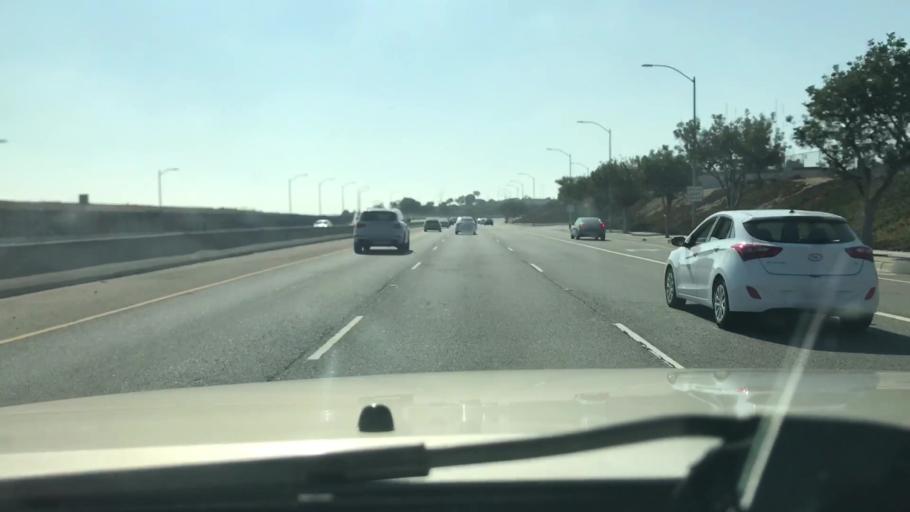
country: US
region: California
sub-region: Los Angeles County
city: El Segundo
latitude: 33.9534
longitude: -118.4066
